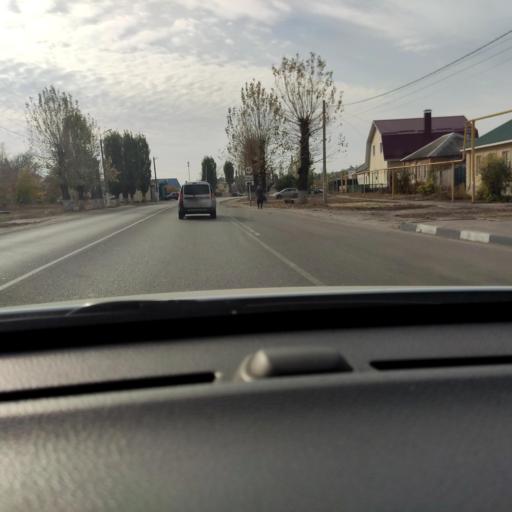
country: RU
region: Voronezj
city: Novaya Usman'
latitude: 51.6168
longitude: 39.3943
